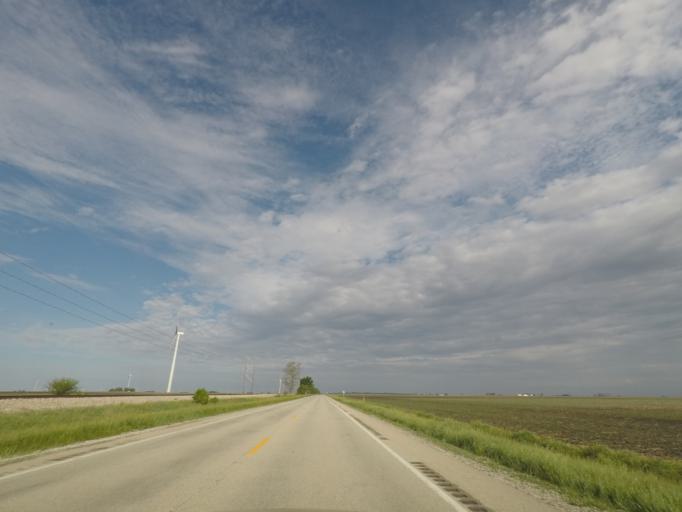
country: US
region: Illinois
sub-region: Logan County
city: Mount Pulaski
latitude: 39.9863
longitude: -89.2264
